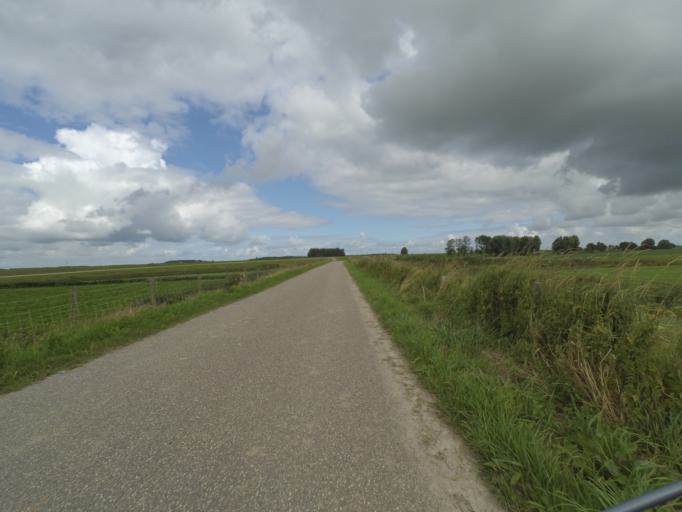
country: NL
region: Groningen
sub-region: Gemeente Zuidhorn
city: Grijpskerk
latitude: 53.3115
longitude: 6.2635
